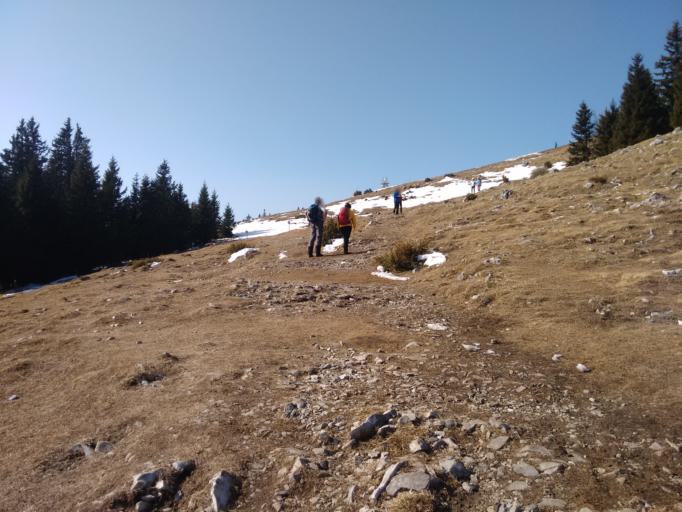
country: AT
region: Styria
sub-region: Politischer Bezirk Graz-Umgebung
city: Sankt Radegund bei Graz
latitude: 47.1969
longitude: 15.4670
